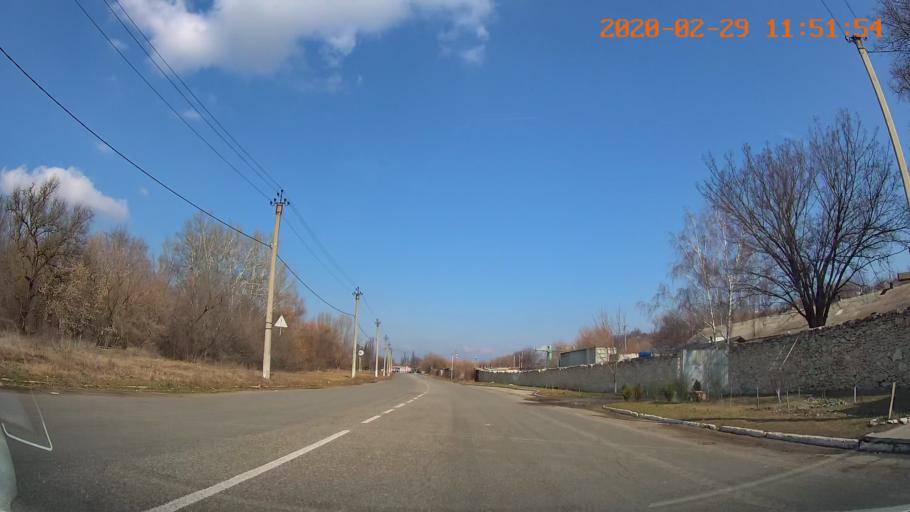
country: MD
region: Telenesti
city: Ribnita
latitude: 47.7677
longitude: 28.9910
